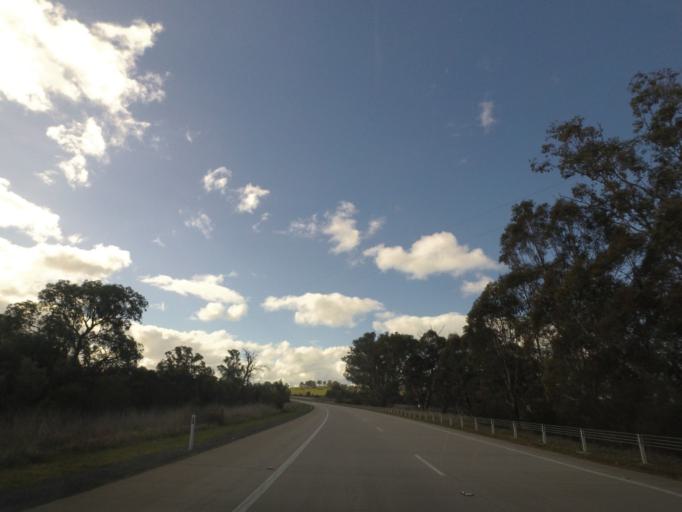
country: AU
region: New South Wales
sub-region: Greater Hume Shire
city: Holbrook
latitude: -35.8719
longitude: 147.1843
